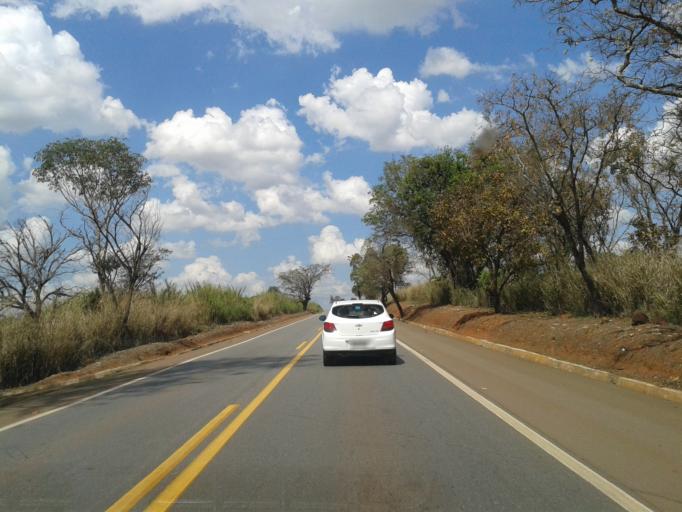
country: BR
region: Minas Gerais
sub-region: Luz
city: Luz
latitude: -19.7745
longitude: -45.7607
